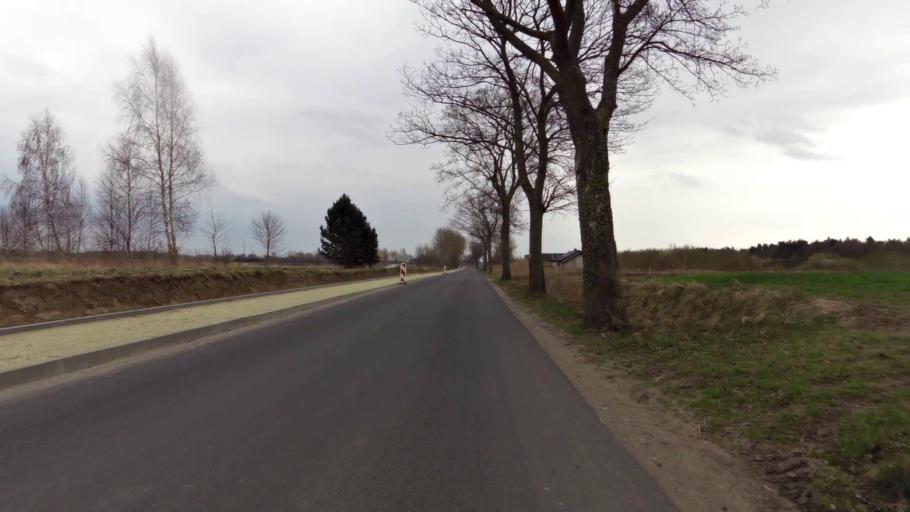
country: PL
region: West Pomeranian Voivodeship
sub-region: Powiat koszalinski
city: Sianow
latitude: 54.2807
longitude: 16.2195
